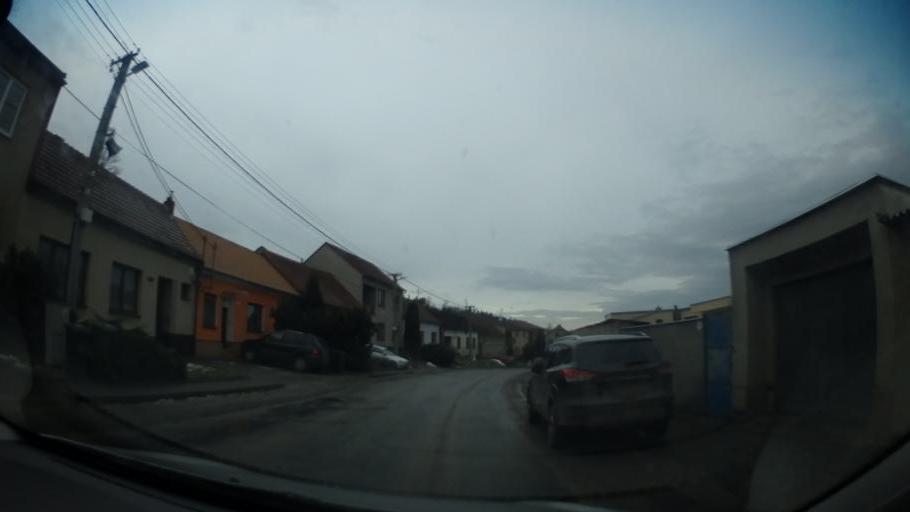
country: CZ
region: South Moravian
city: Strelice
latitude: 49.1337
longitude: 16.4761
